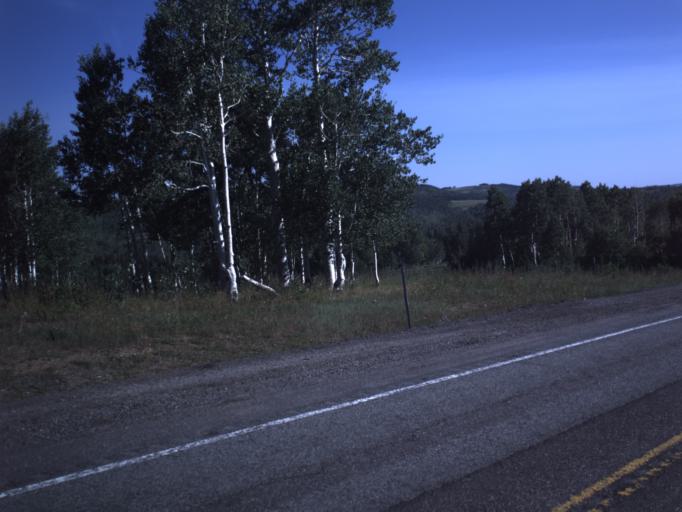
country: US
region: Utah
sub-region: Sanpete County
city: Fairview
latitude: 39.6691
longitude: -111.3259
